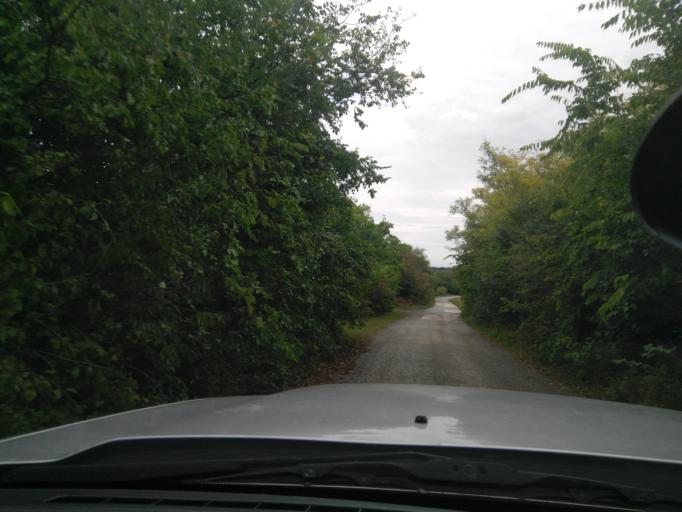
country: HU
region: Fejer
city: Martonvasar
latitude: 47.3522
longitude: 18.7726
